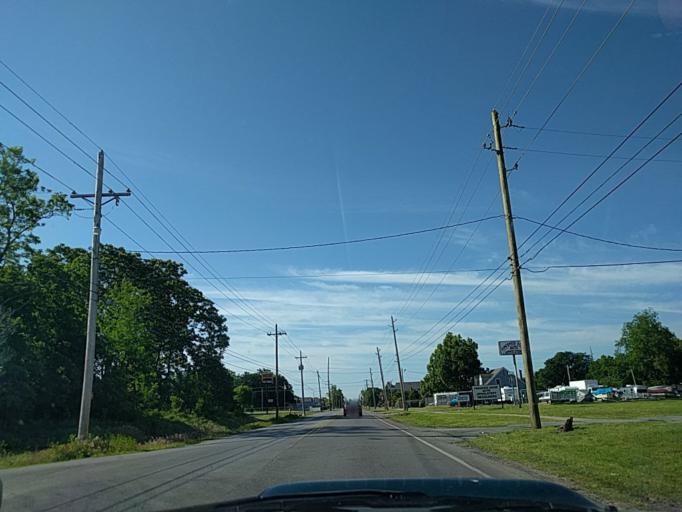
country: US
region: Oklahoma
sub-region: Tulsa County
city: Jenks
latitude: 36.0699
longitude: -95.9758
